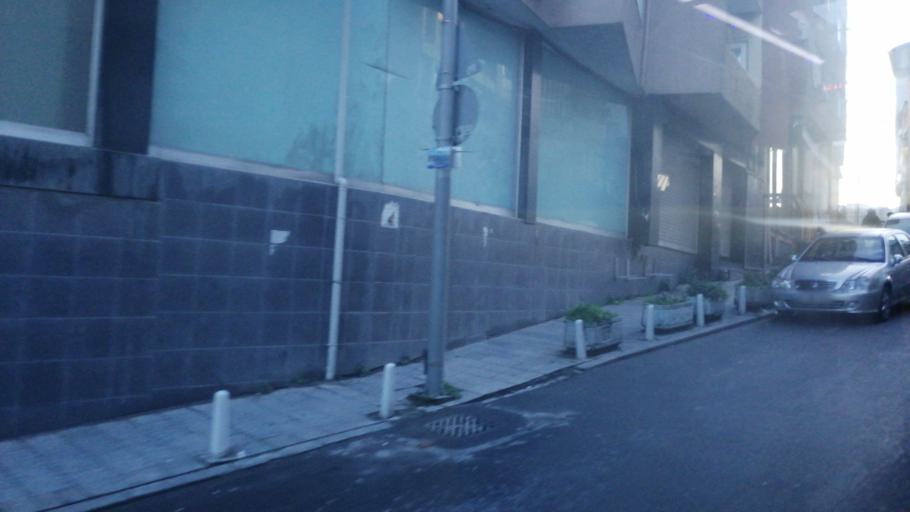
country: TR
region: Istanbul
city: Sisli
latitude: 41.0878
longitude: 28.9850
